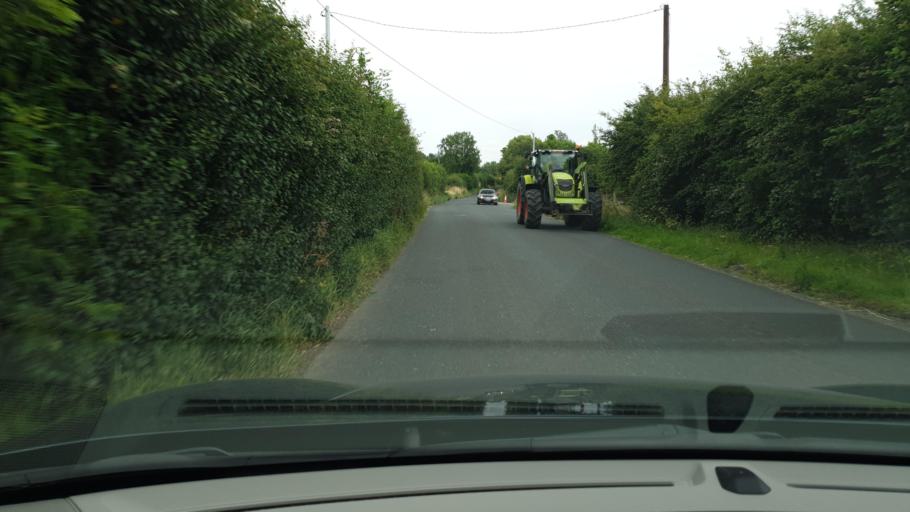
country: IE
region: Leinster
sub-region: An Mhi
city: Ashbourne
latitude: 53.5345
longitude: -6.4012
